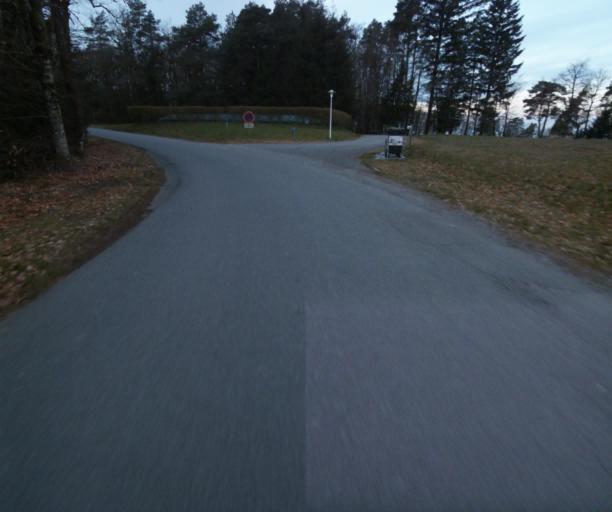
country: FR
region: Limousin
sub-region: Departement de la Correze
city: Correze
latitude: 45.4292
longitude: 1.8368
